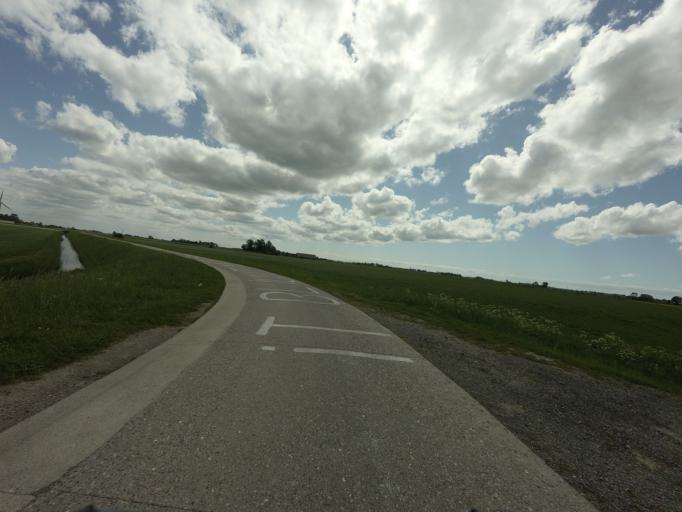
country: NL
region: Friesland
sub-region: Gemeente Franekeradeel
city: Tzum
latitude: 53.1237
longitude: 5.5544
